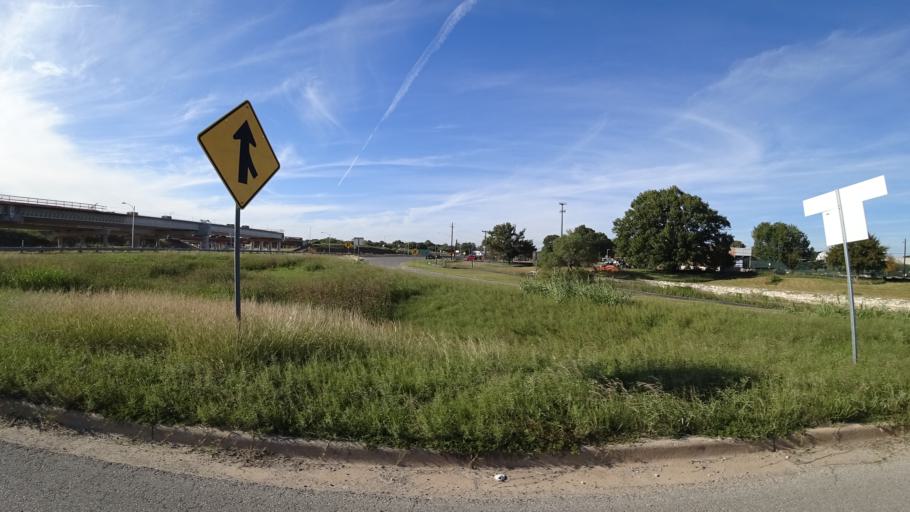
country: US
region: Texas
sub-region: Travis County
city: Austin
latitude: 30.2502
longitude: -97.6908
